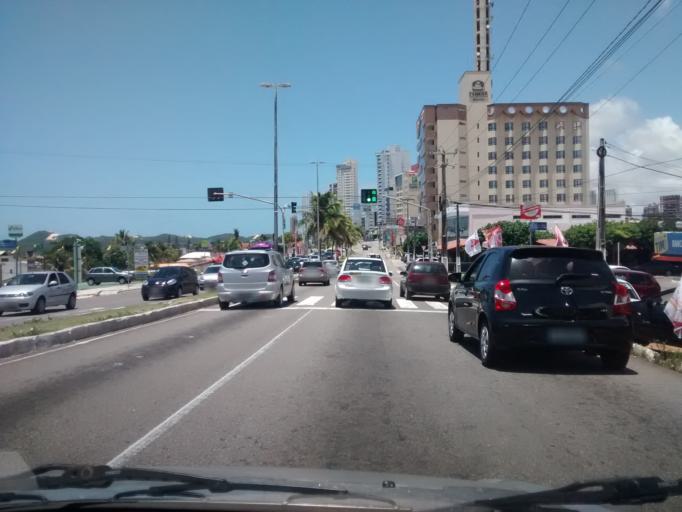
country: BR
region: Rio Grande do Norte
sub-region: Natal
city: Natal
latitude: -5.8698
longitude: -35.1817
